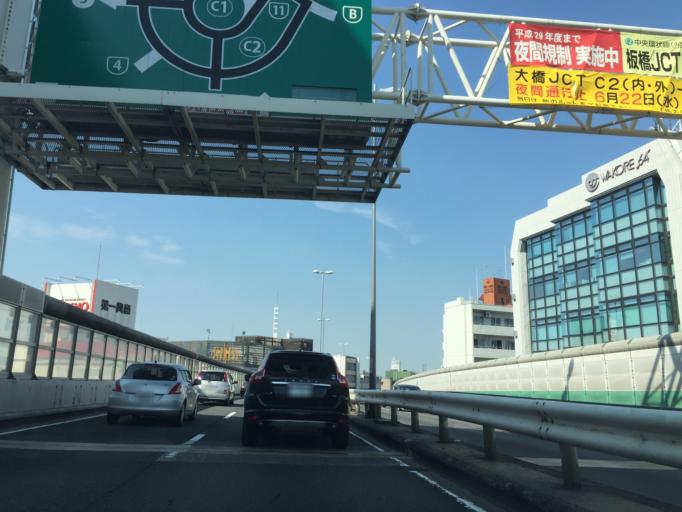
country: JP
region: Tokyo
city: Tokyo
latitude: 35.6428
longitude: 139.6704
